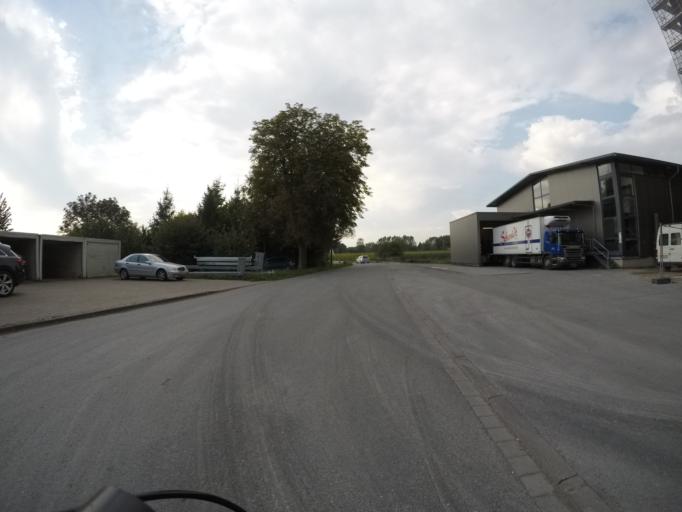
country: DE
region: North Rhine-Westphalia
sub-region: Regierungsbezirk Detmold
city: Herford
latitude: 52.0620
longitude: 8.6126
